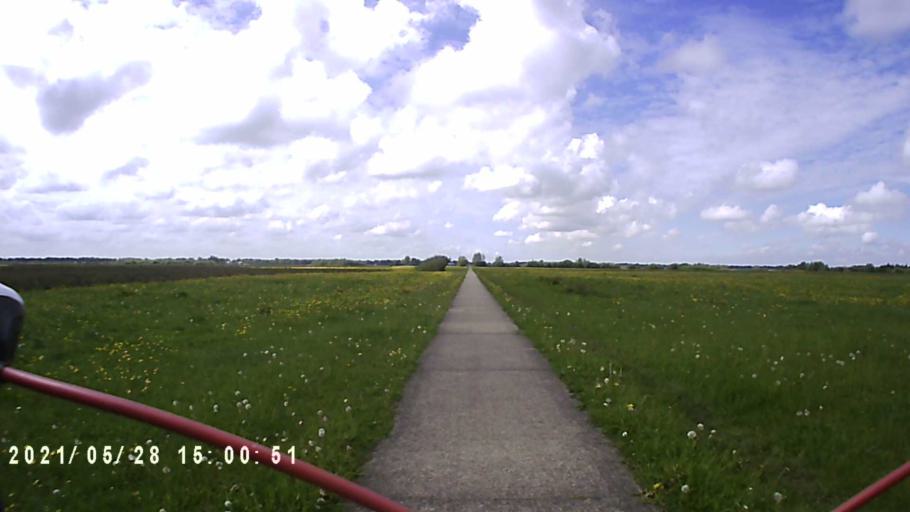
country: NL
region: Groningen
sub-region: Gemeente Hoogezand-Sappemeer
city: Hoogezand
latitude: 53.1955
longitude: 6.7416
